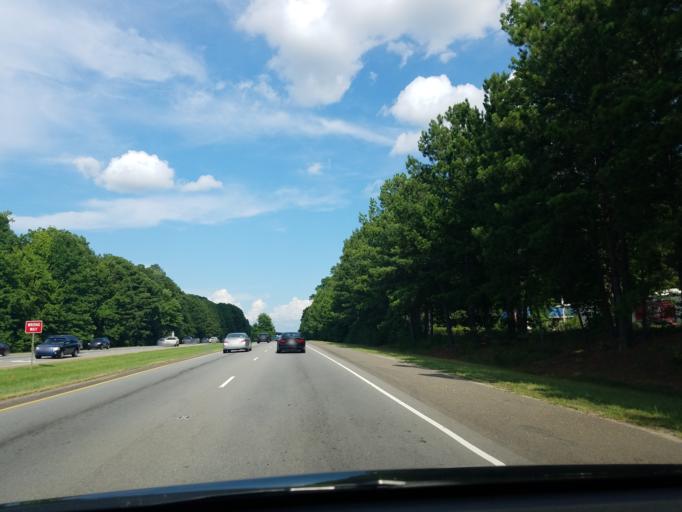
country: US
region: North Carolina
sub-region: Wake County
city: Apex
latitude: 35.7435
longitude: -78.8207
